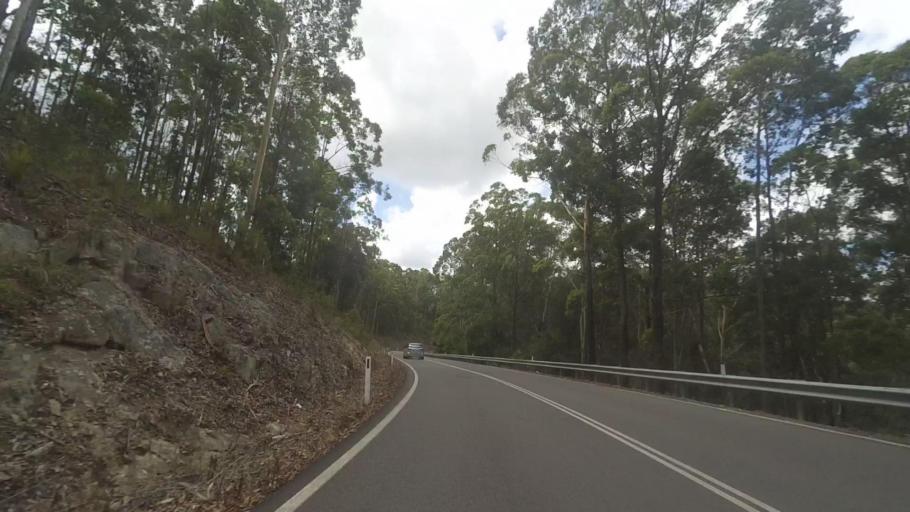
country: AU
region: New South Wales
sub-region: Great Lakes
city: Bulahdelah
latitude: -32.3909
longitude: 152.2474
